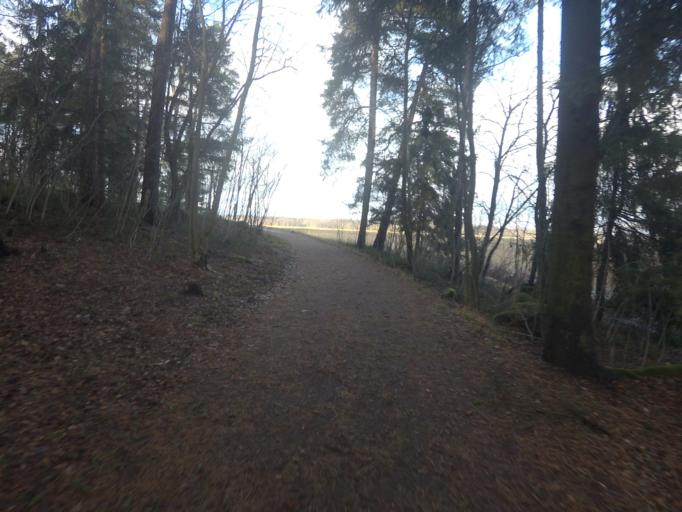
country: FI
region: Uusimaa
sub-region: Helsinki
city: Teekkarikylae
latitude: 60.1917
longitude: 24.8331
